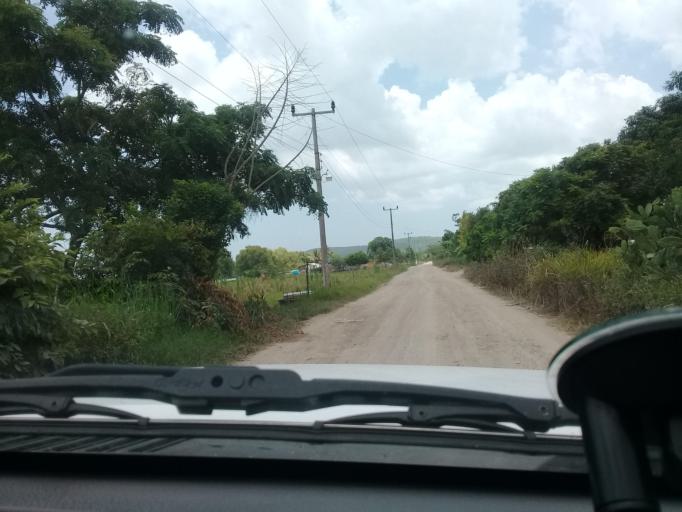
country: MX
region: Veracruz
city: Panuco
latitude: 22.1282
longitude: -98.0580
